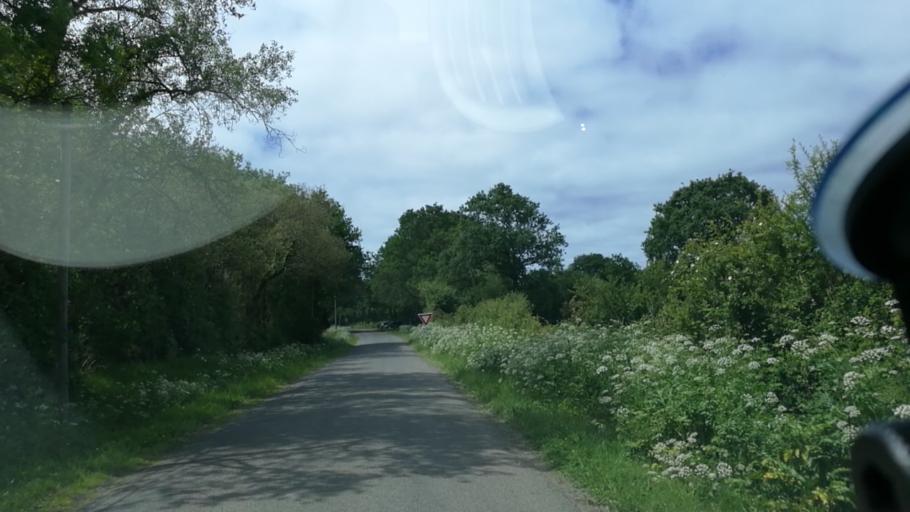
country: FR
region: Pays de la Loire
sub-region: Departement de la Loire-Atlantique
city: Asserac
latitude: 47.4408
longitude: -2.4263
